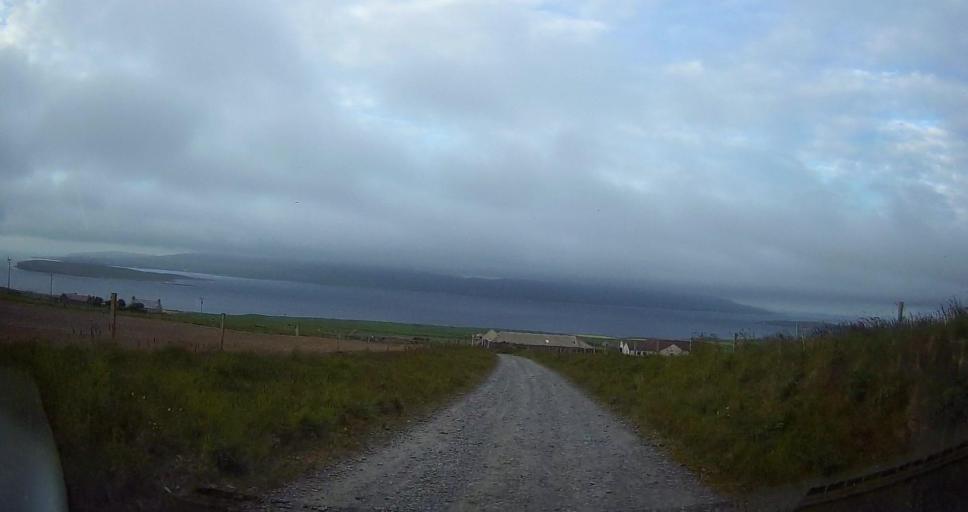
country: GB
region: Scotland
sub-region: Orkney Islands
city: Orkney
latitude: 59.1203
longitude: -3.1343
